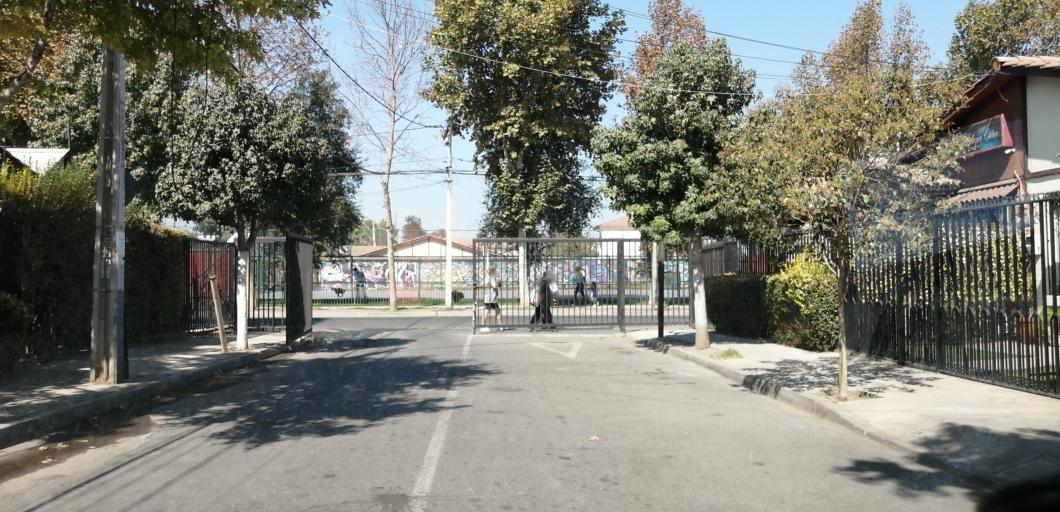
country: CL
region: Santiago Metropolitan
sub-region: Provincia de Santiago
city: Lo Prado
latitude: -33.4547
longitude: -70.7475
